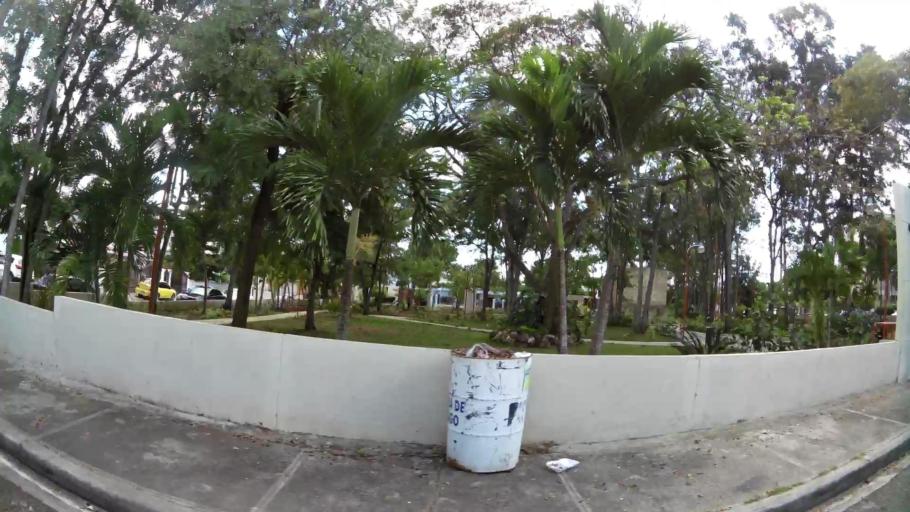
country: DO
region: Santiago
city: Santiago de los Caballeros
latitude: 19.4551
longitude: -70.6785
